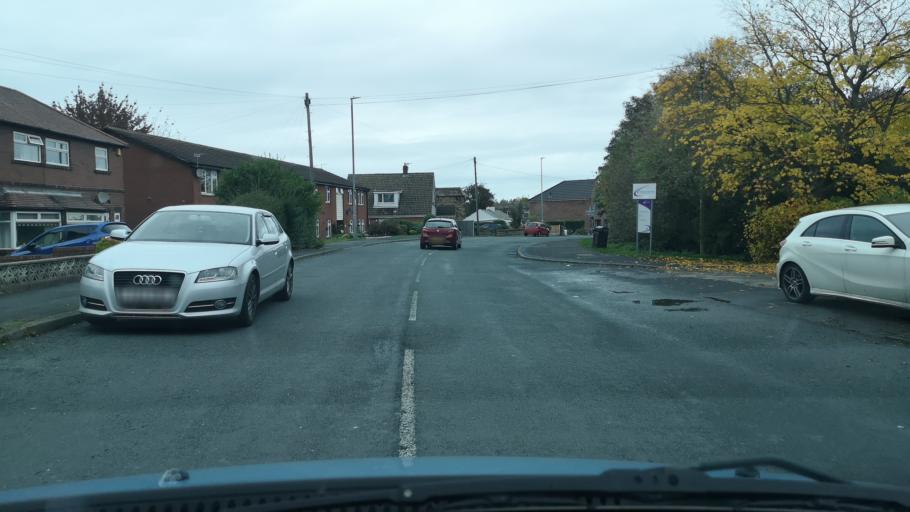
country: GB
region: England
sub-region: Kirklees
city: Heckmondwike
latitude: 53.7209
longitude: -1.6675
